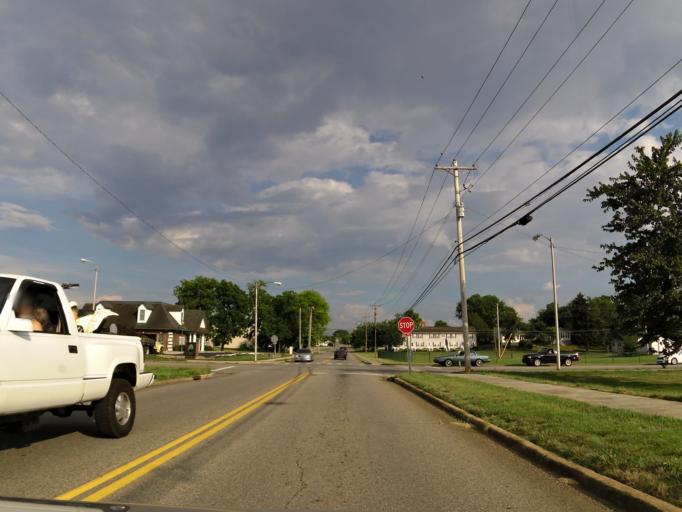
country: US
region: Tennessee
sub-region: Blount County
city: Maryville
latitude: 35.7680
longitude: -83.9763
